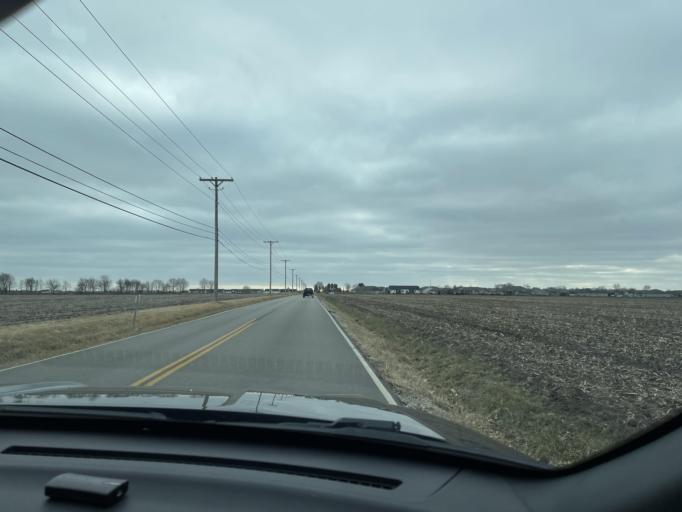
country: US
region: Illinois
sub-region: Sangamon County
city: Jerome
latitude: 39.7703
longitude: -89.7534
